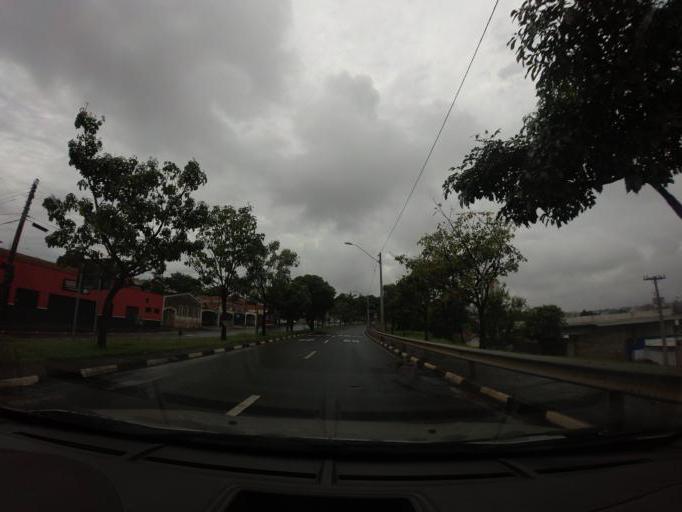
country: BR
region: Sao Paulo
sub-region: Piracicaba
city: Piracicaba
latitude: -22.7400
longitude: -47.6459
